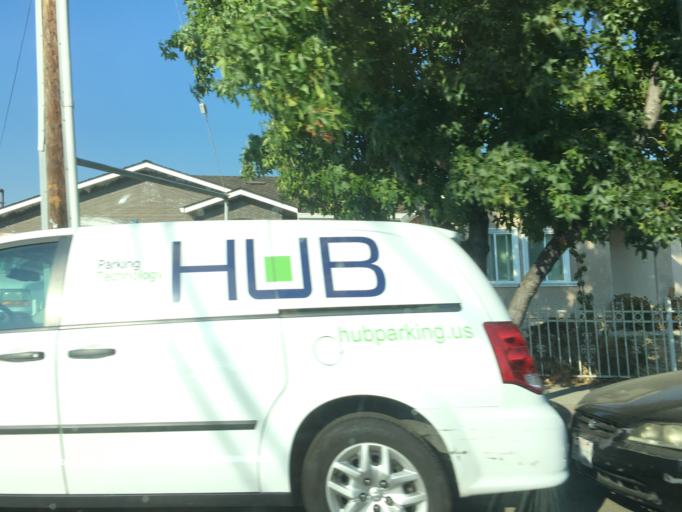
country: US
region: California
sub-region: Santa Clara County
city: Alum Rock
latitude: 37.3728
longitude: -121.8337
